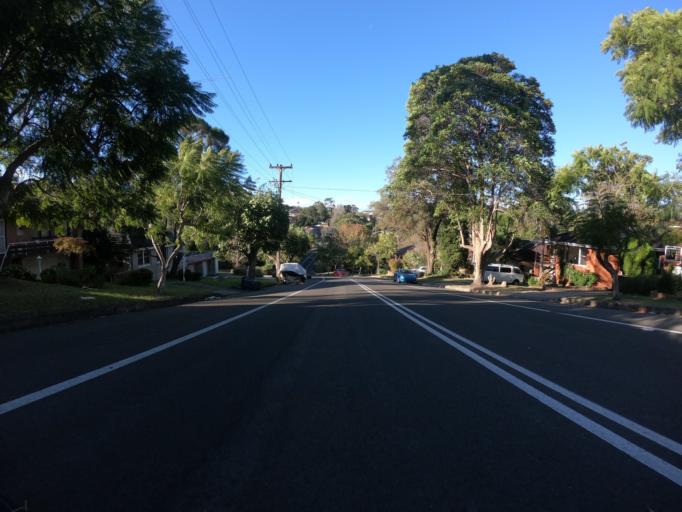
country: AU
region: New South Wales
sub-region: Wollongong
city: Mount Keira
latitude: -34.4250
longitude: 150.8473
